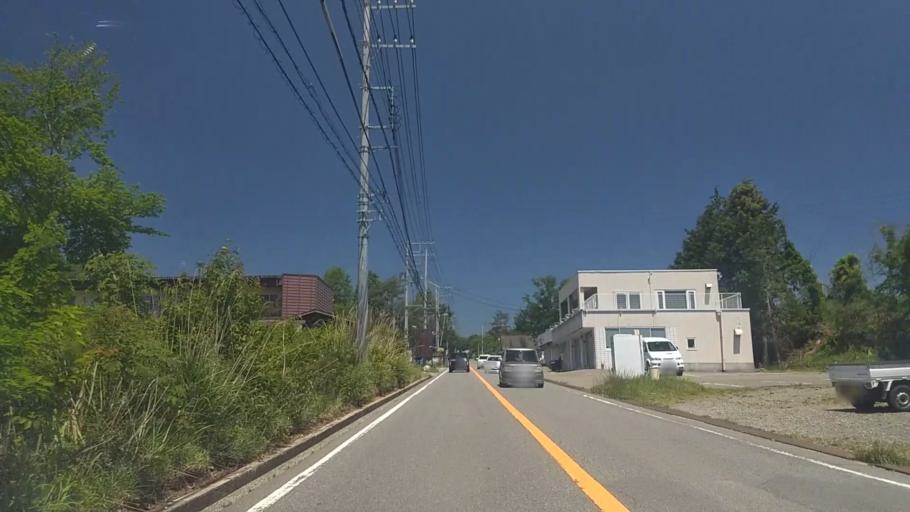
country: JP
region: Yamanashi
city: Nirasaki
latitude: 35.8478
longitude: 138.4326
